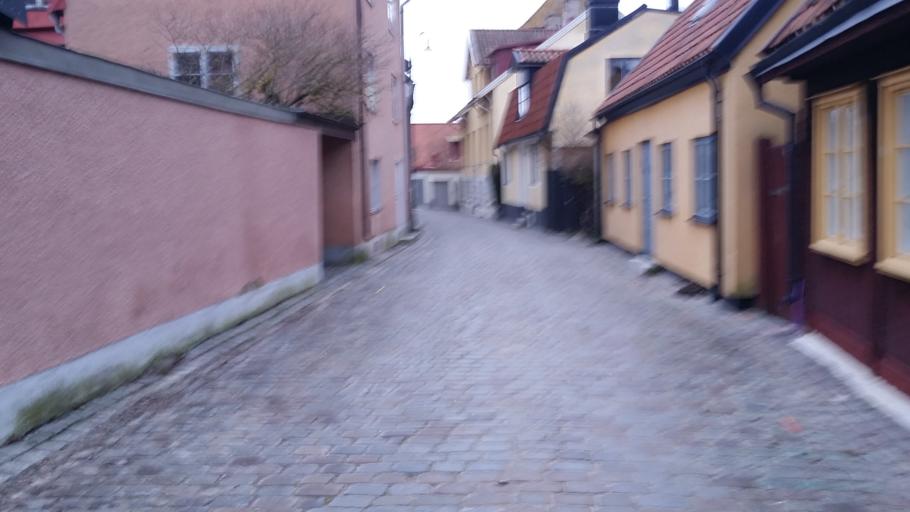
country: SE
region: Gotland
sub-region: Gotland
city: Visby
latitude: 57.6430
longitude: 18.2922
